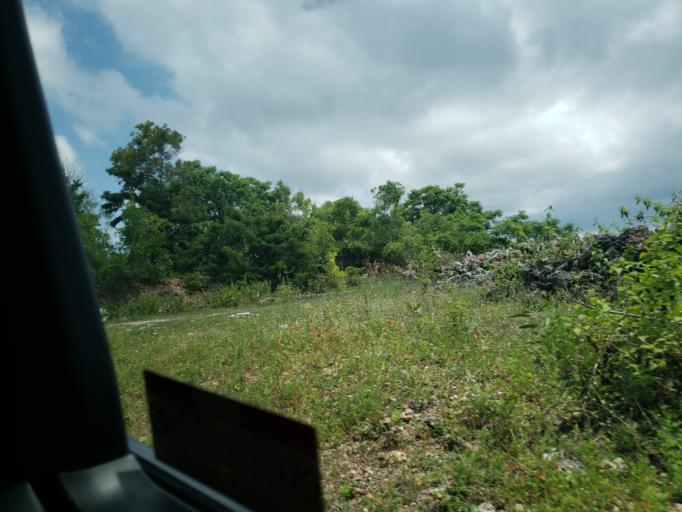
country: ID
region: Bali
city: Kangin
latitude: -8.8440
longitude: 115.1470
